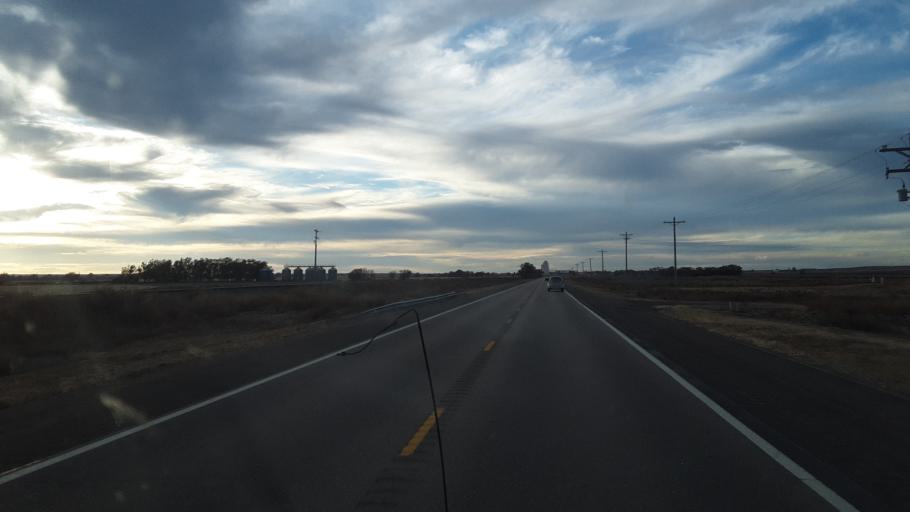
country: US
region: Kansas
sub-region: Hamilton County
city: Syracuse
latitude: 38.0340
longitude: -101.9794
